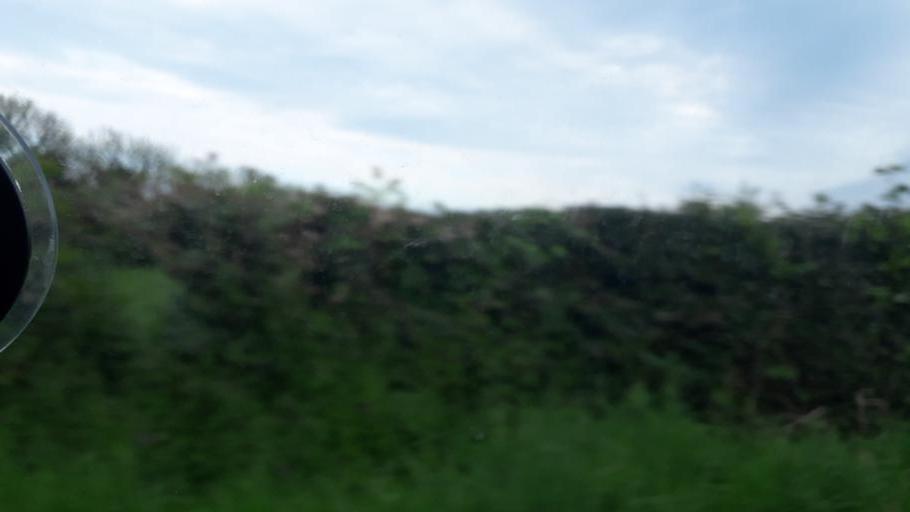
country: IE
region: Leinster
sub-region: Kildare
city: Celbridge
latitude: 53.3206
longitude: -6.5491
